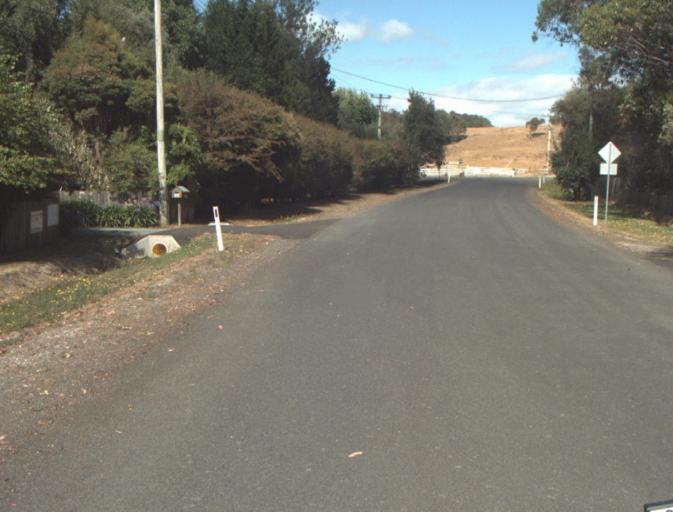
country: AU
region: Tasmania
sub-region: Launceston
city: Mayfield
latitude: -41.2610
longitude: 147.1601
